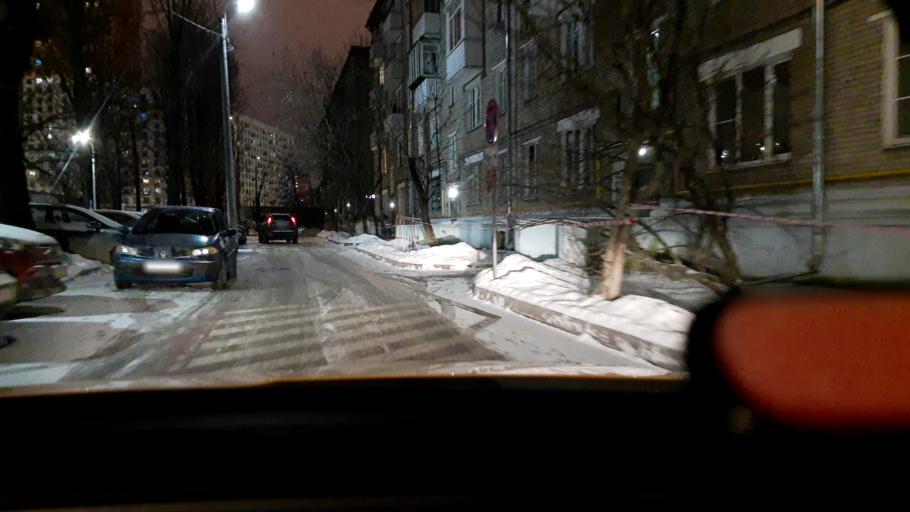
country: RU
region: Moscow
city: Mikhalkovo
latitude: 55.6643
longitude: 37.4192
